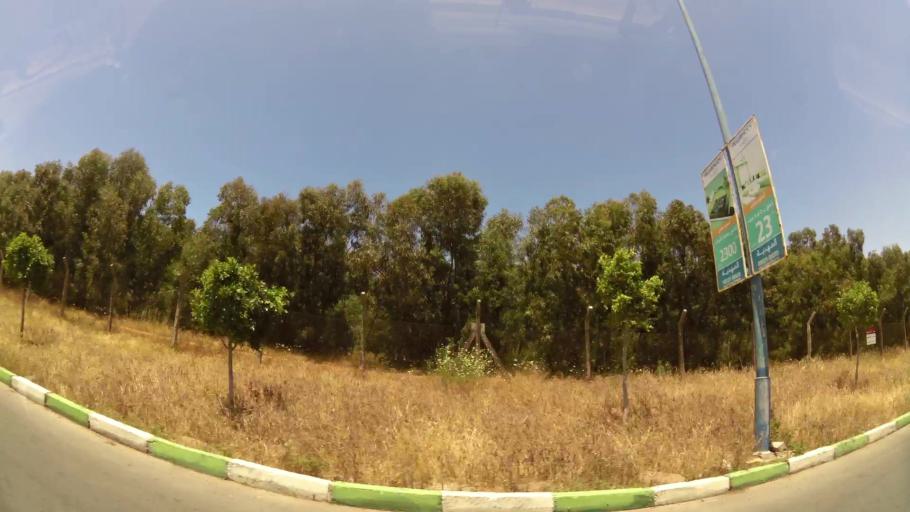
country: MA
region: Gharb-Chrarda-Beni Hssen
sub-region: Kenitra Province
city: Kenitra
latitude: 34.2711
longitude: -6.6353
